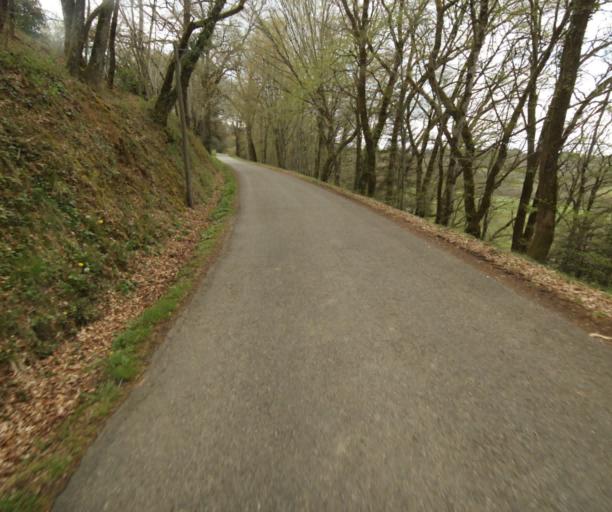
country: FR
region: Limousin
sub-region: Departement de la Correze
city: Laguenne
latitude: 45.2482
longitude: 1.8494
